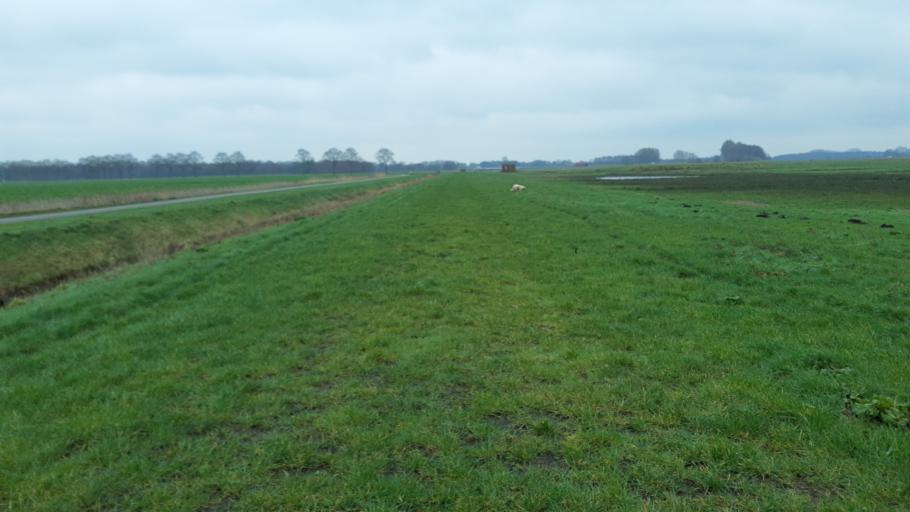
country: NL
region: Groningen
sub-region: Gemeente Veendam
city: Veendam
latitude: 53.0425
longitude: 6.8069
